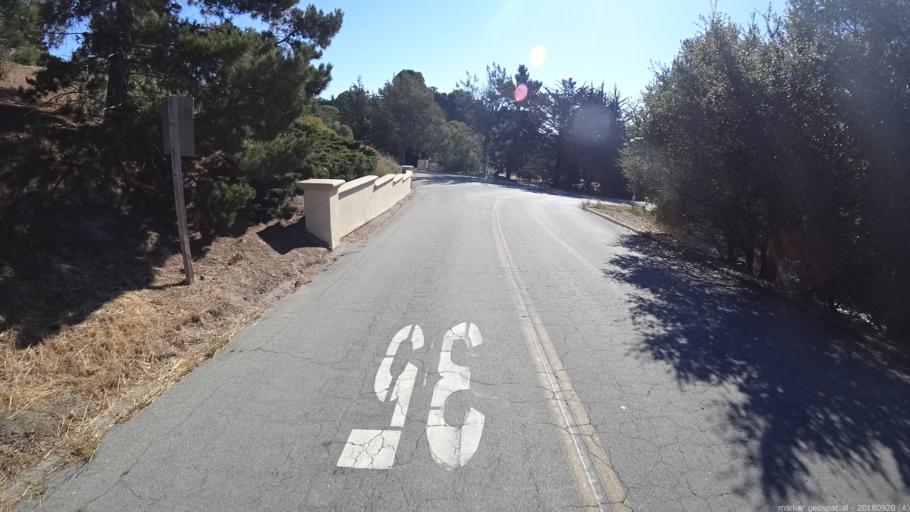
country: US
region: California
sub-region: Monterey County
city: Carmel-by-the-Sea
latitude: 36.5451
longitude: -121.9005
